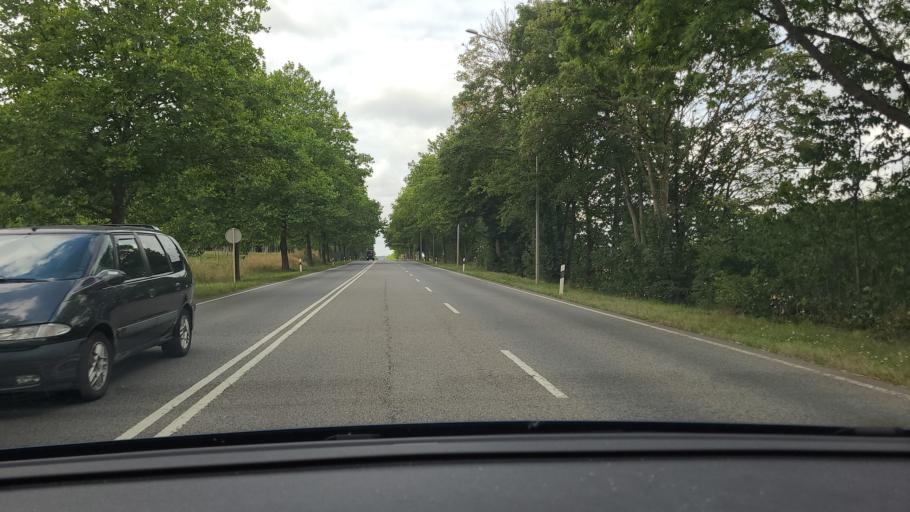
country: LU
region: Luxembourg
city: Schouweiler
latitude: 49.5740
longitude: 5.9381
